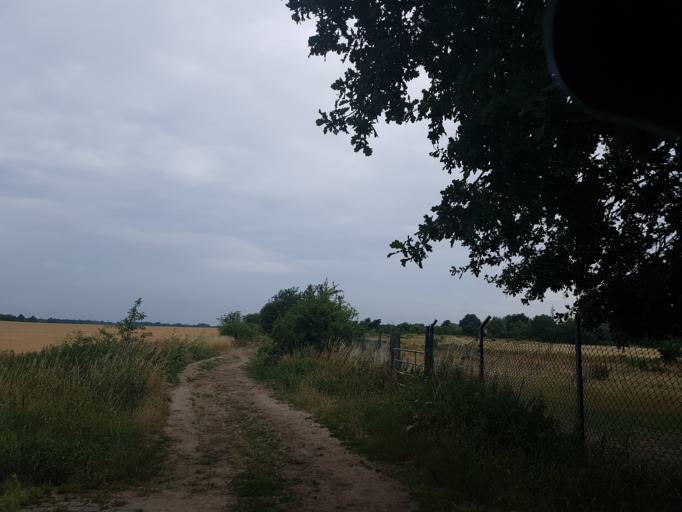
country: DE
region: Brandenburg
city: Stahnsdorf
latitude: 52.3753
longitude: 13.2392
